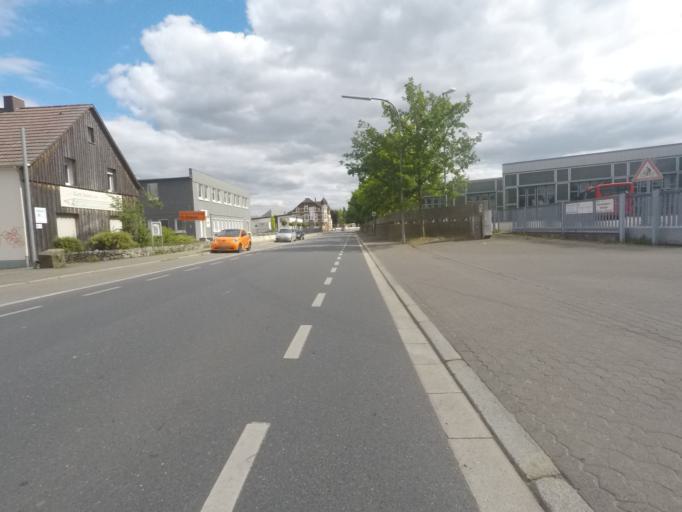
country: DE
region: North Rhine-Westphalia
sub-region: Regierungsbezirk Detmold
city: Herford
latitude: 52.1277
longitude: 8.6693
